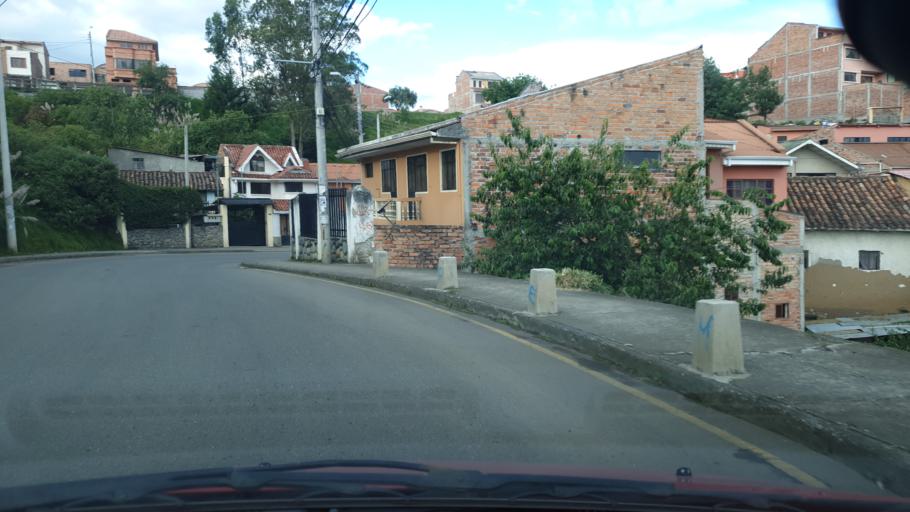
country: EC
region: Azuay
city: Cuenca
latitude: -2.8878
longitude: -79.0132
